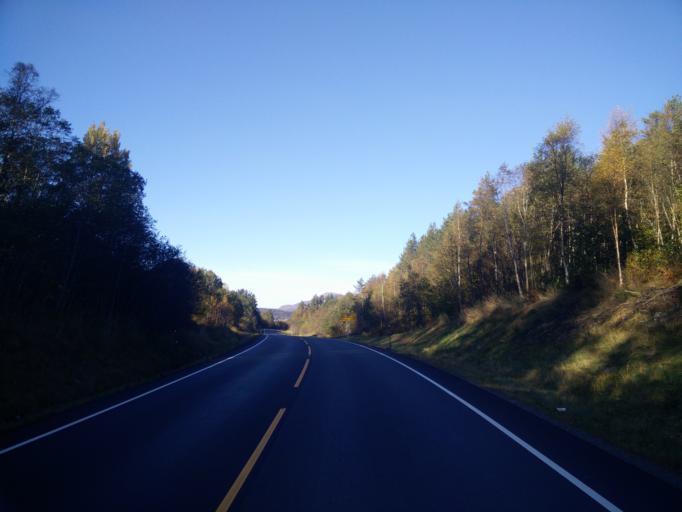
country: NO
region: More og Romsdal
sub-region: Halsa
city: Liaboen
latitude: 63.0912
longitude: 8.3516
